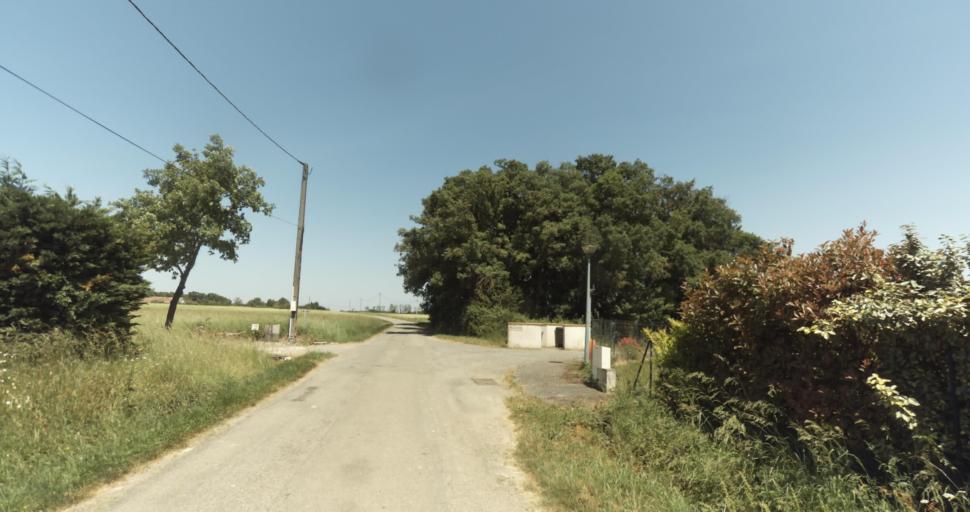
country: FR
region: Midi-Pyrenees
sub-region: Departement de la Haute-Garonne
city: Levignac
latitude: 43.6384
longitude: 1.1885
